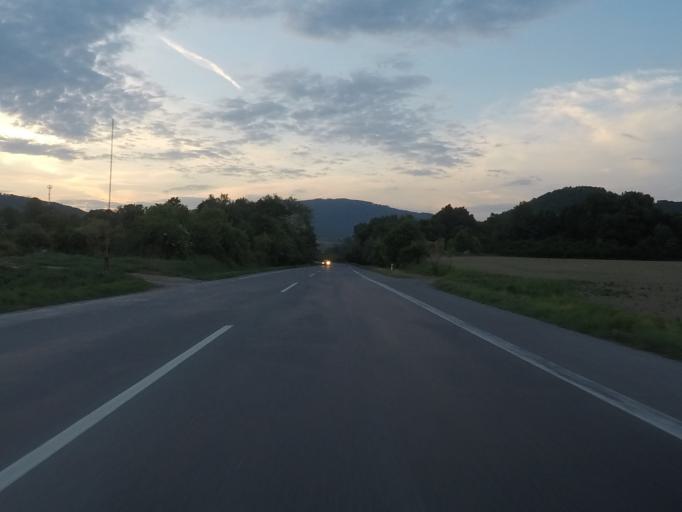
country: SK
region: Banskobystricky
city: Rimavska Sobota
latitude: 48.4909
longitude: 19.9417
